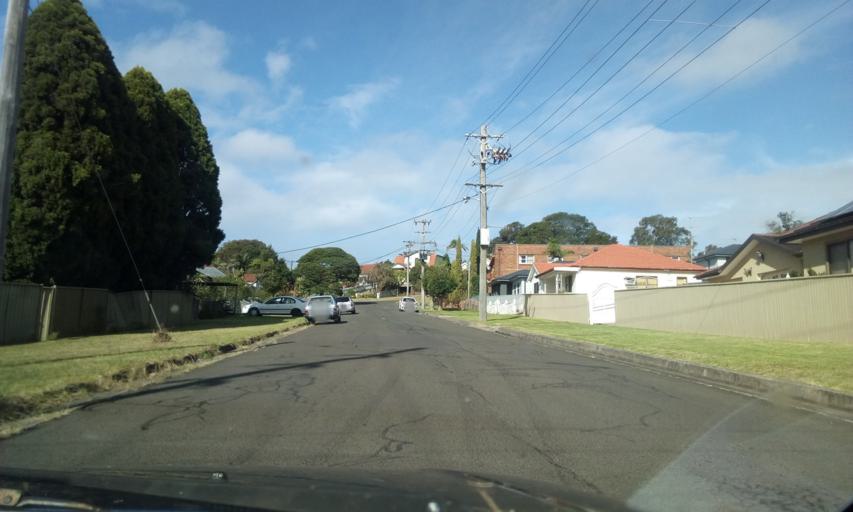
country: AU
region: New South Wales
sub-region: Wollongong
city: Port Kembla
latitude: -34.4817
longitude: 150.8986
